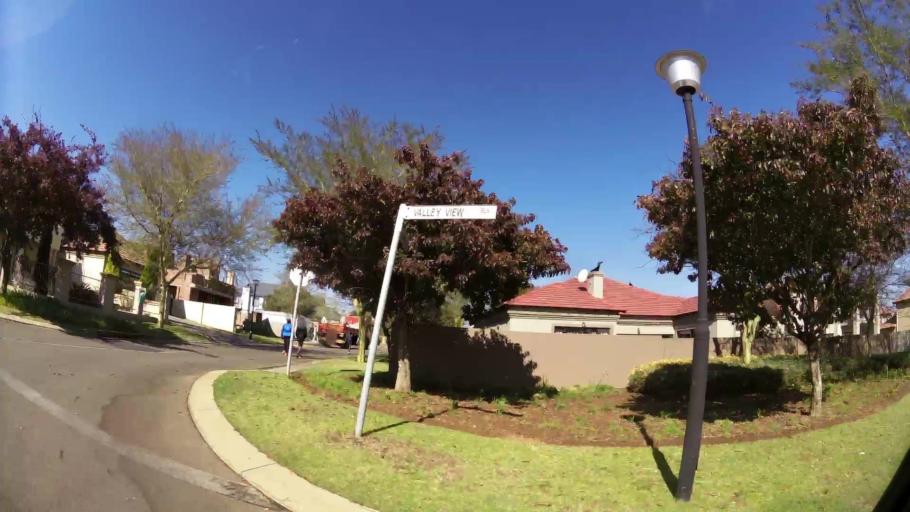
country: ZA
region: Gauteng
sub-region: City of Johannesburg Metropolitan Municipality
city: Midrand
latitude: -25.9353
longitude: 28.1325
